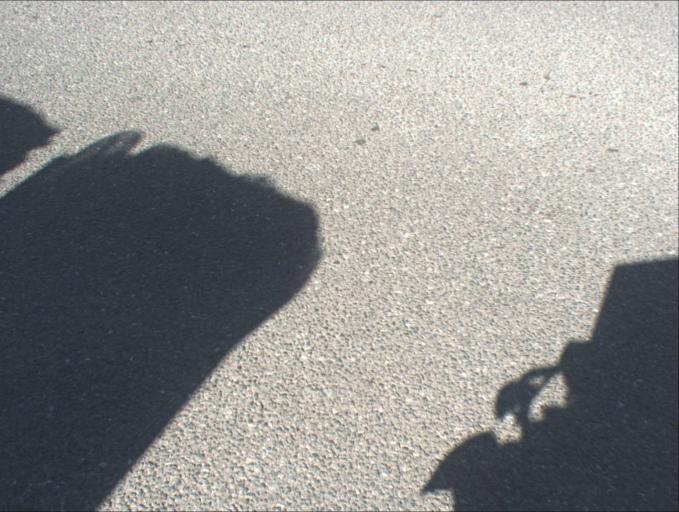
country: AU
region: Queensland
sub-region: Logan
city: Beenleigh
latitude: -27.7144
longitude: 153.1816
